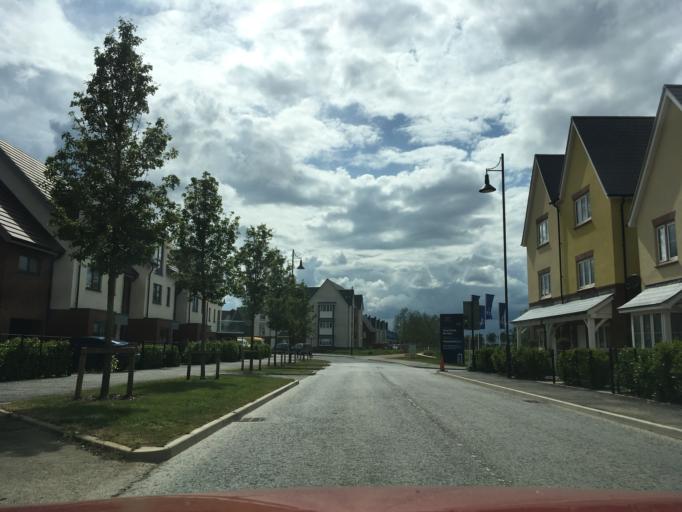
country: GB
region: England
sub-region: Borough of Swindon
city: Broad Blunsdon
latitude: 51.6107
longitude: -1.8237
